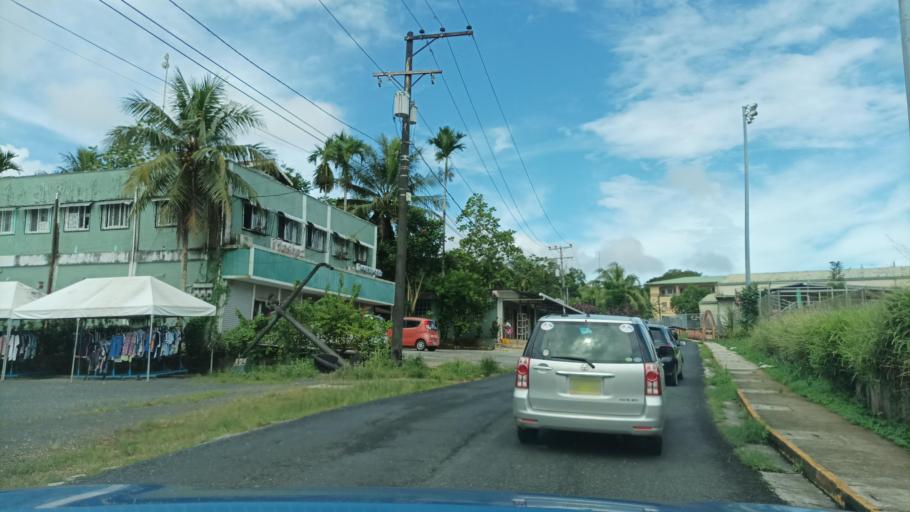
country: FM
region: Pohnpei
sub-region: Kolonia Municipality
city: Kolonia
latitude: 6.9589
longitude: 158.2122
